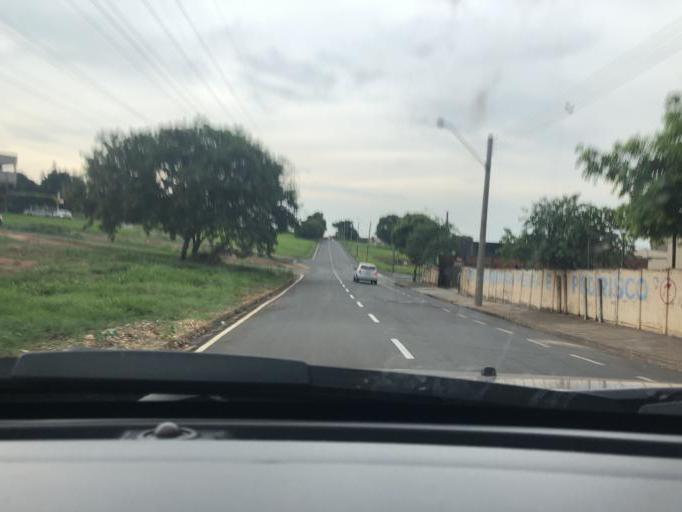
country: BR
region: Sao Paulo
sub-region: Sao Jose Do Rio Preto
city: Sao Jose do Rio Preto
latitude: -20.8444
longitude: -49.3837
